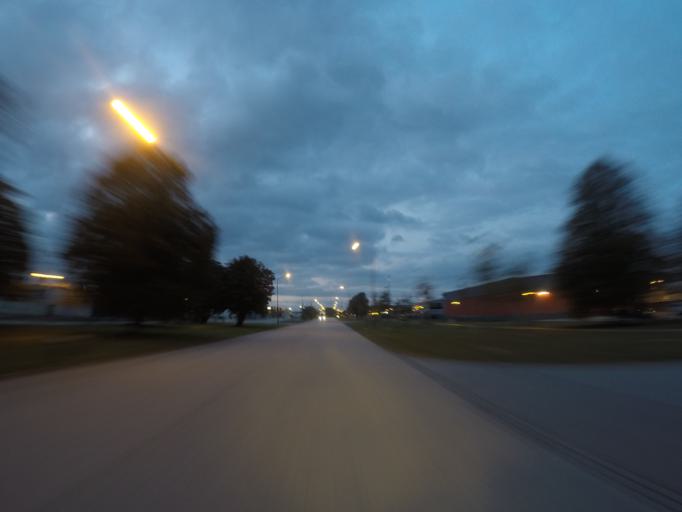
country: SE
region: Skane
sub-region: Malmo
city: Malmoe
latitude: 55.6169
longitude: 13.0322
